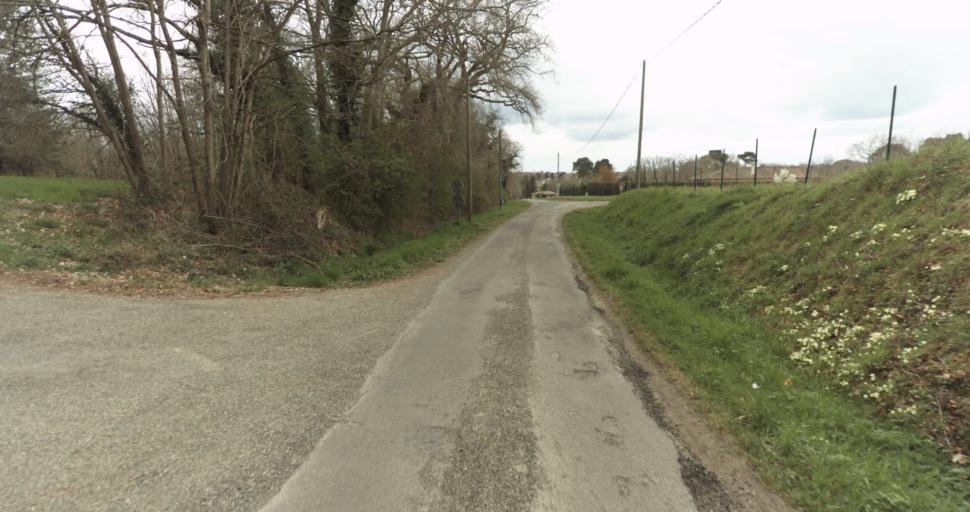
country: FR
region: Aquitaine
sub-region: Departement des Landes
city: Sarbazan
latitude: 44.0278
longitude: -0.3163
